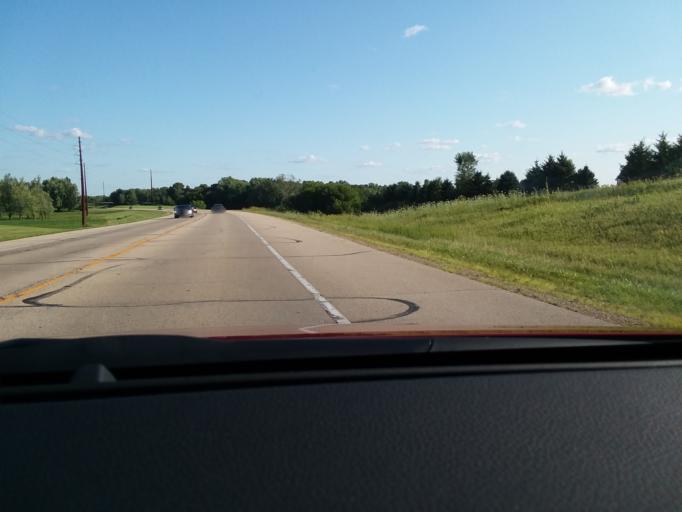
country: US
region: Wisconsin
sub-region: Dane County
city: Waunakee
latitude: 43.1753
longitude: -89.4117
